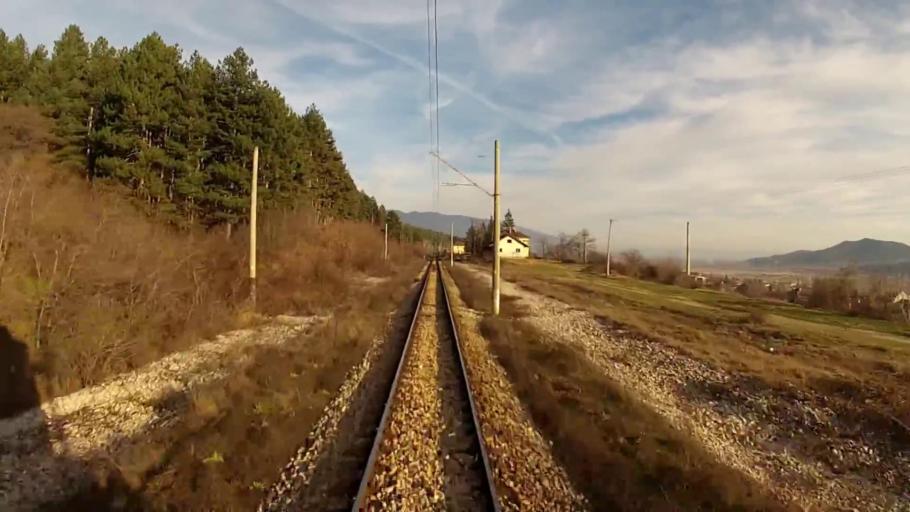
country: BG
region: Plovdiv
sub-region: Obshtina Karlovo
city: Klisura
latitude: 42.7230
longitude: 24.5897
